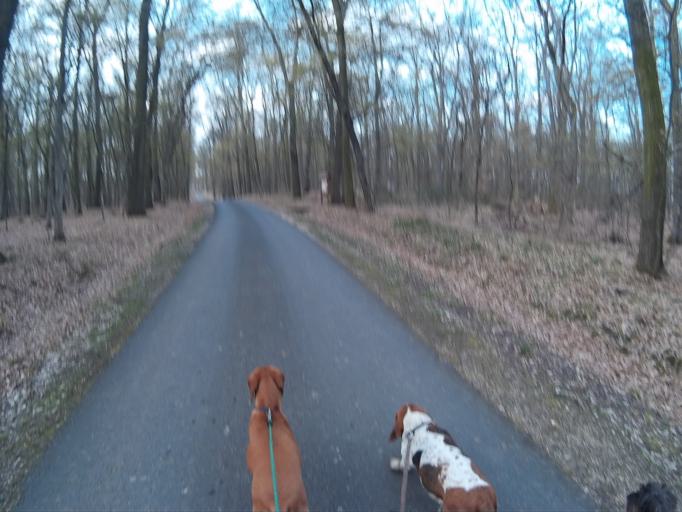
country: HU
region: Vas
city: Sarvar
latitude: 47.1964
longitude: 16.9992
